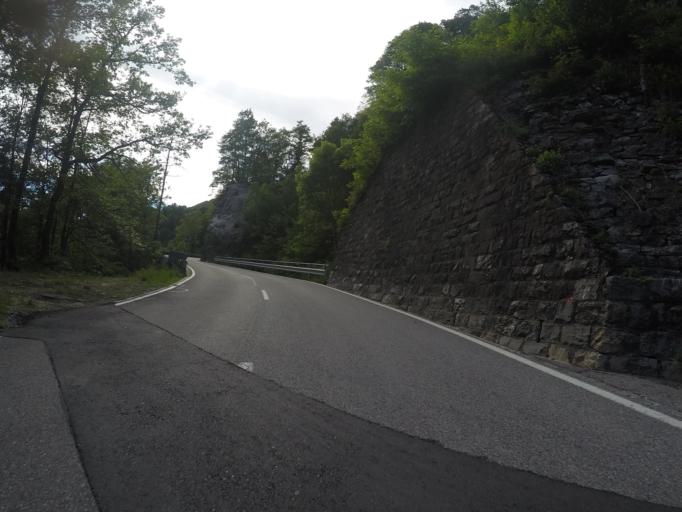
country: IT
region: Piedmont
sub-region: Provincia Verbano-Cusio-Ossola
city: Cursolo
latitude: 46.1609
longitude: 8.6311
